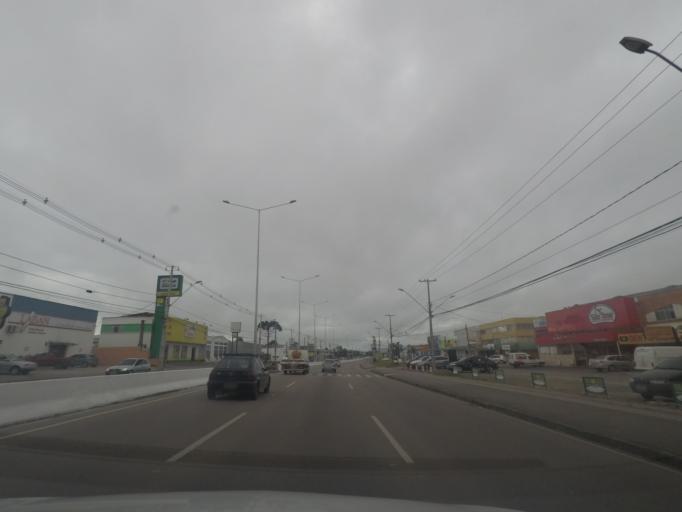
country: BR
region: Parana
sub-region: Pinhais
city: Pinhais
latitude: -25.4345
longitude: -49.1738
